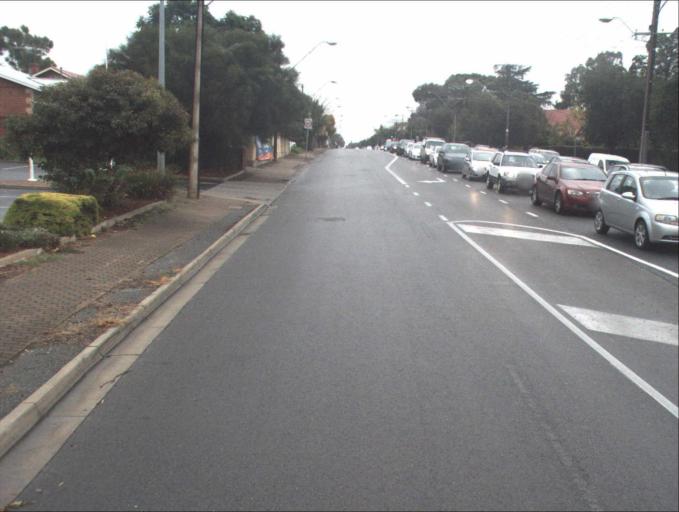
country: AU
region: South Australia
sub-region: Port Adelaide Enfield
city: Klemzig
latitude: -34.8838
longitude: 138.6199
